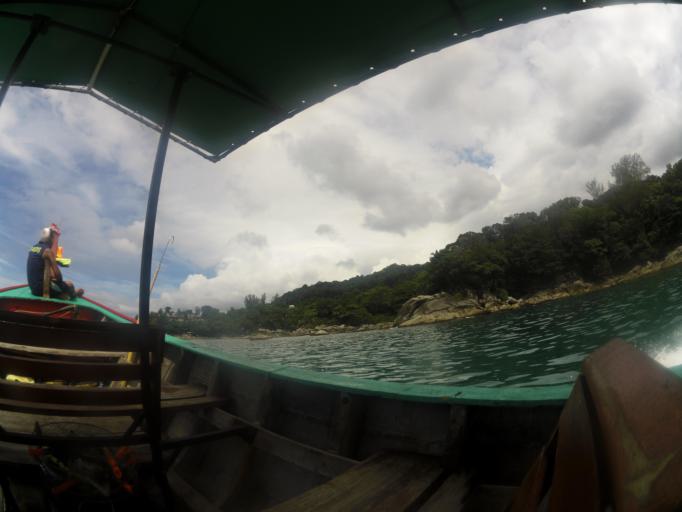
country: TH
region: Phuket
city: Patong
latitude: 7.9656
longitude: 98.2786
